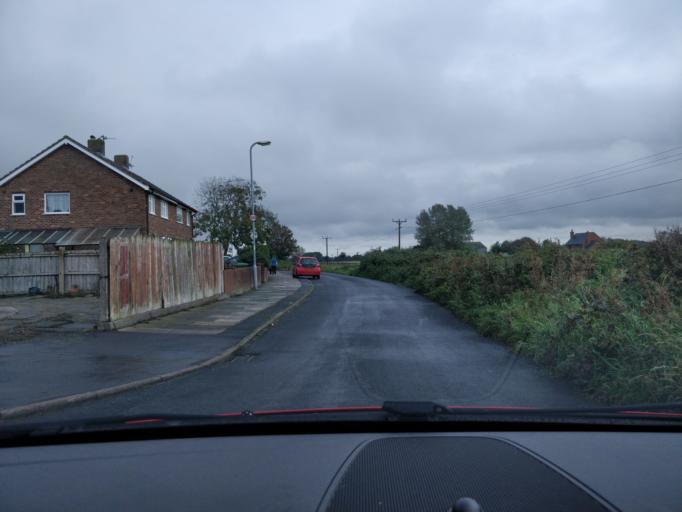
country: GB
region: England
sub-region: Sefton
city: Southport
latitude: 53.6065
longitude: -3.0218
